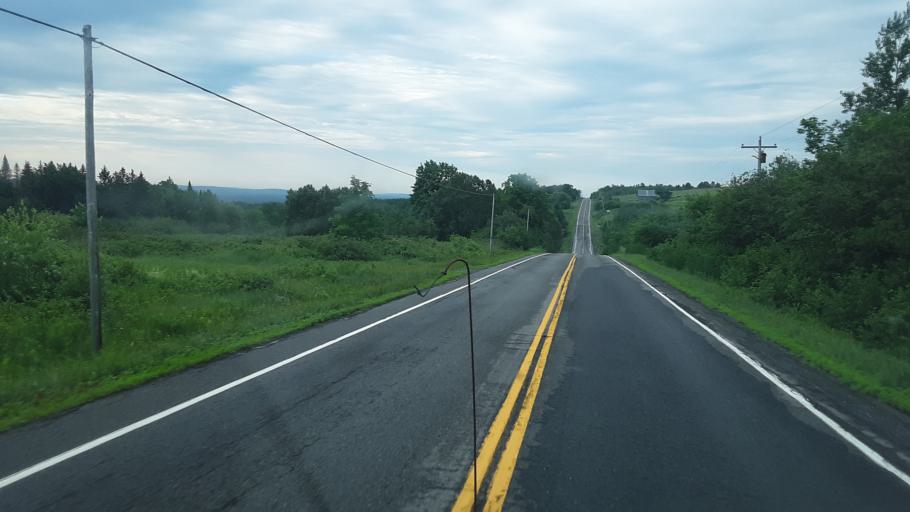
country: US
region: Maine
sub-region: Penobscot County
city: Patten
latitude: 46.0386
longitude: -68.4441
